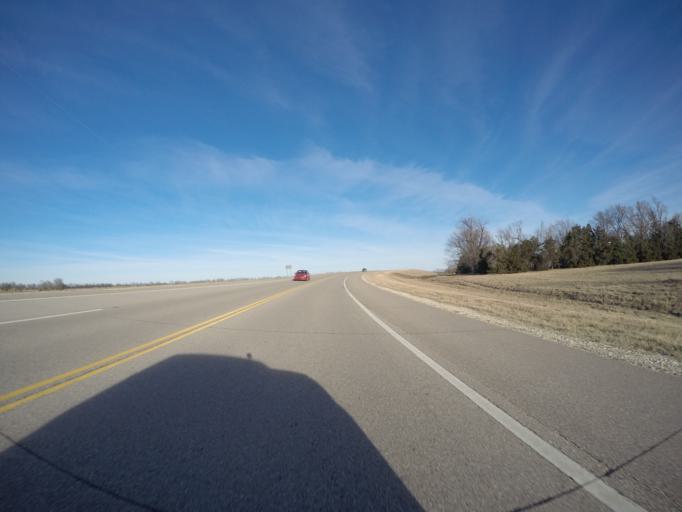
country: US
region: Kansas
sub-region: Marion County
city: Peabody
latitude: 38.1758
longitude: -97.1152
